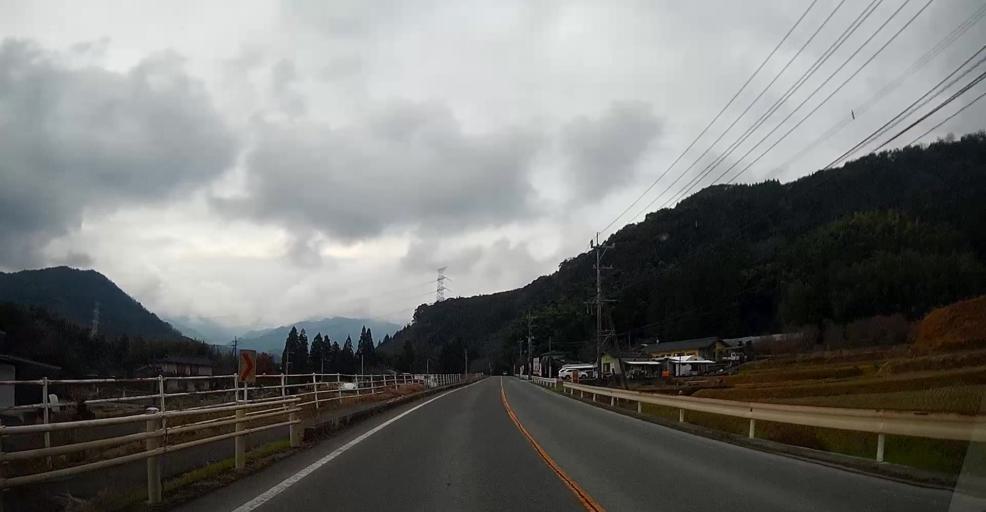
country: JP
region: Kumamoto
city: Matsubase
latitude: 32.6312
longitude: 130.8081
